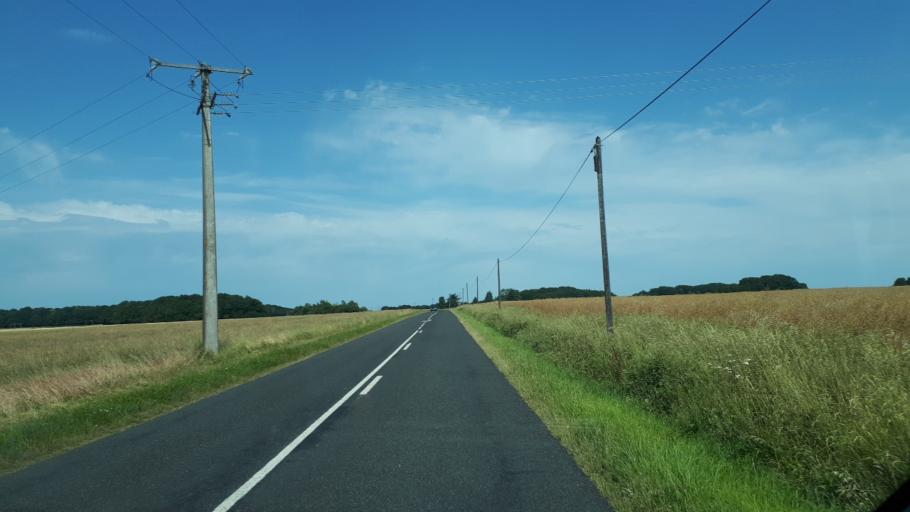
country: FR
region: Centre
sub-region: Departement du Loir-et-Cher
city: La Ville-aux-Clercs
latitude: 47.9648
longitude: 1.0628
